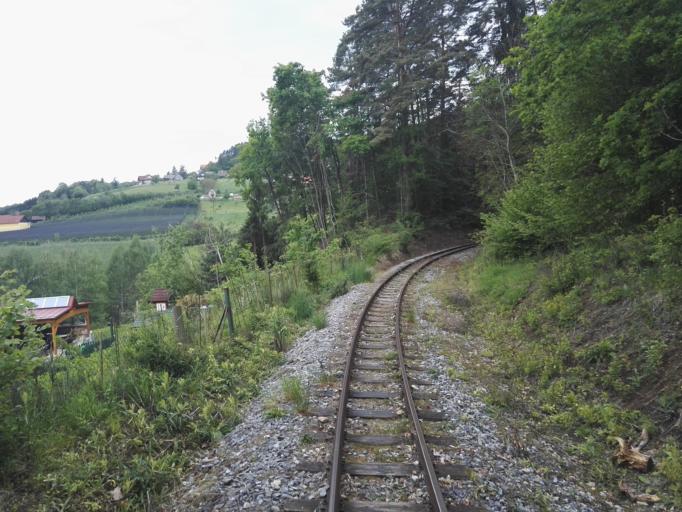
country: AT
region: Styria
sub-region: Politischer Bezirk Weiz
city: Anger
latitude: 47.2386
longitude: 15.6839
